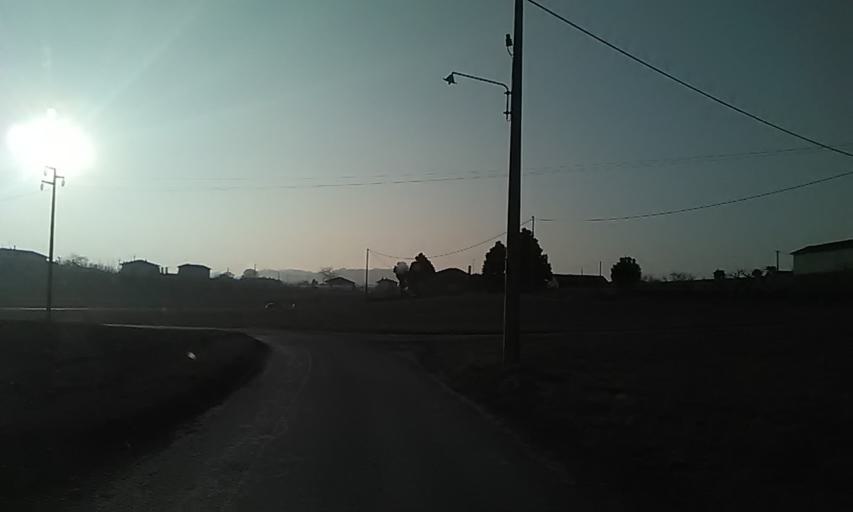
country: IT
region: Piedmont
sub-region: Provincia di Biella
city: Cavaglia
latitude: 45.4025
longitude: 8.1117
